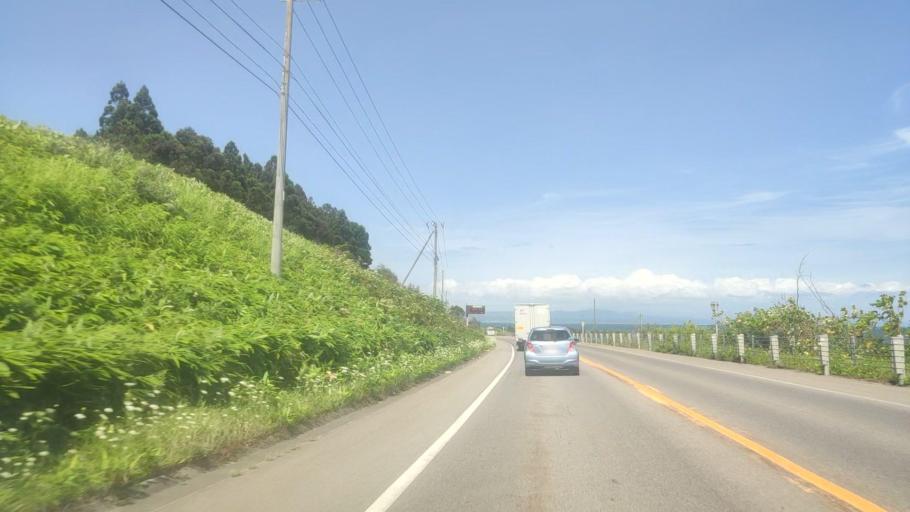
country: JP
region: Hokkaido
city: Nanae
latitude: 42.2058
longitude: 140.4049
